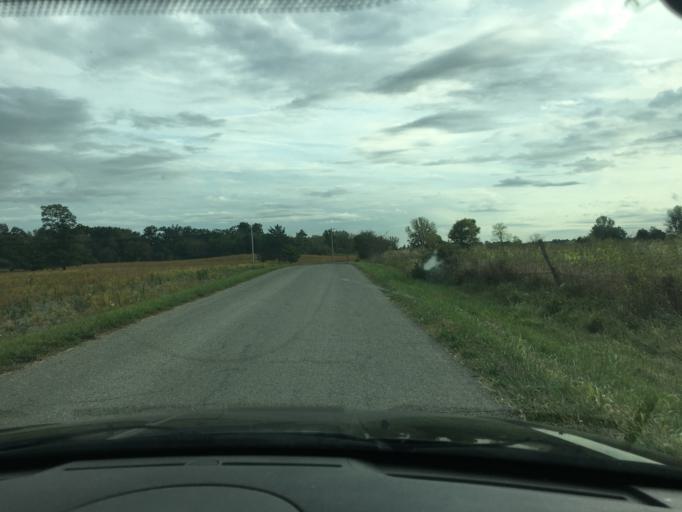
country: US
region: Ohio
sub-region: Logan County
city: Bellefontaine
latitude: 40.3103
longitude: -83.8072
